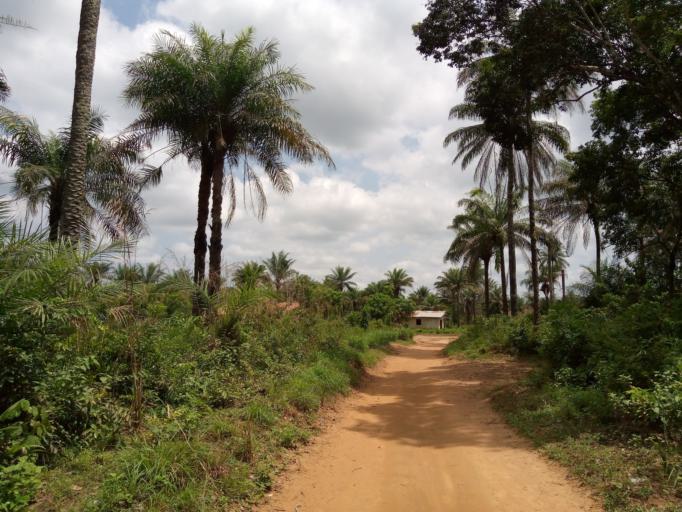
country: SL
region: Western Area
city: Waterloo
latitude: 8.4010
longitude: -12.9486
